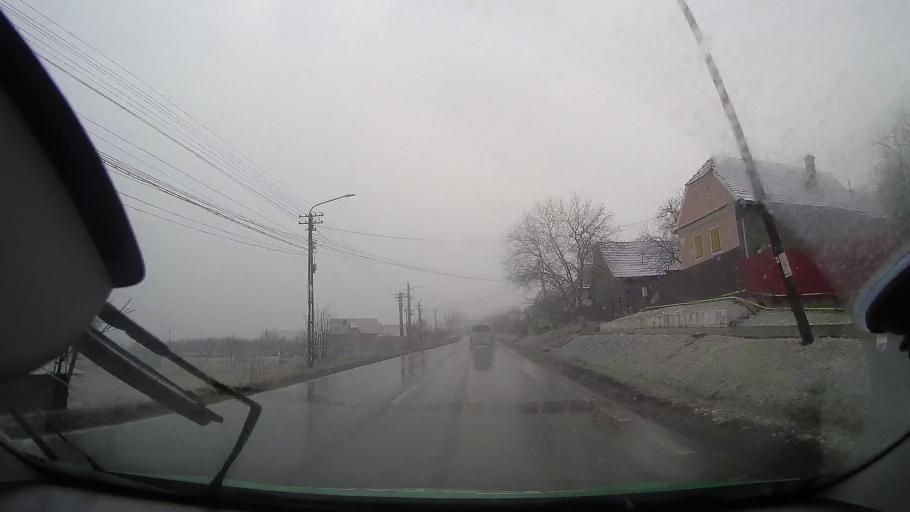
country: RO
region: Mures
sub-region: Comuna Bagaciu
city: Delenii
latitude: 46.2801
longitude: 24.3009
